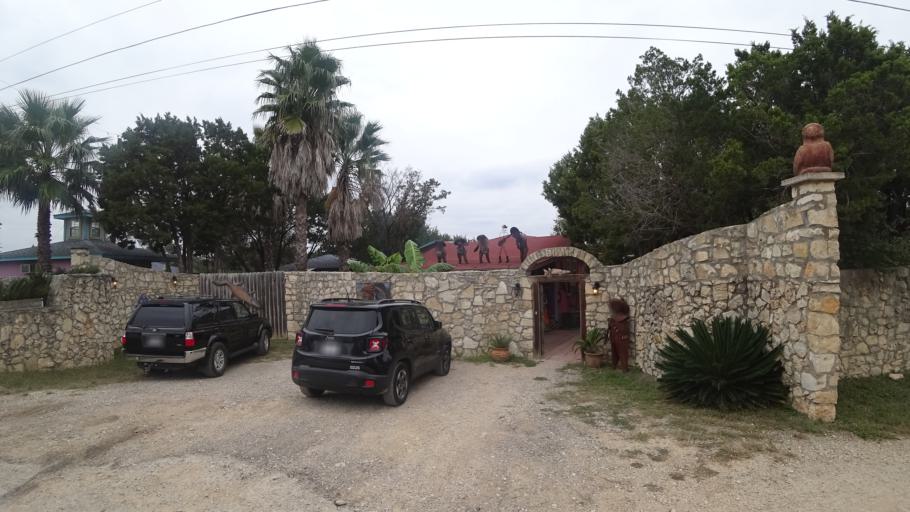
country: US
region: Texas
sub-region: Travis County
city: Hudson Bend
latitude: 30.3826
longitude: -97.9341
